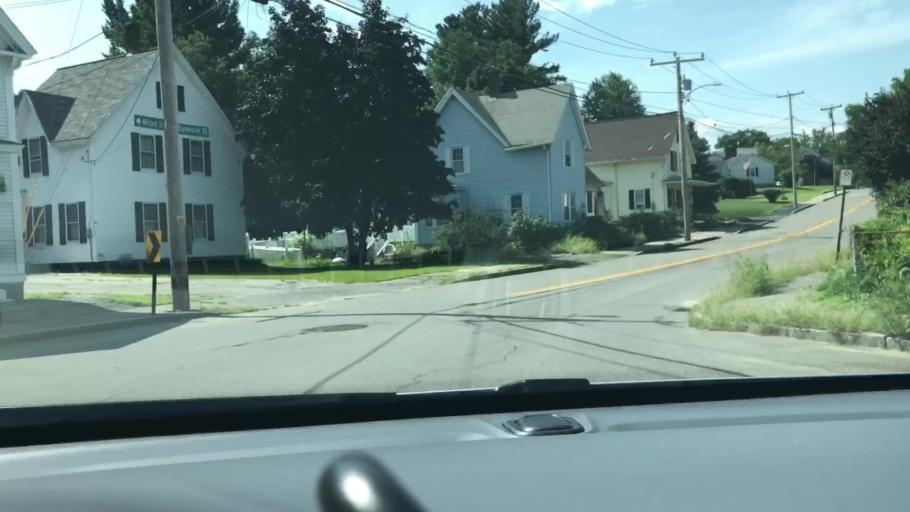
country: US
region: New Hampshire
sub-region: Hillsborough County
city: Pinardville
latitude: 42.9769
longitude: -71.4877
